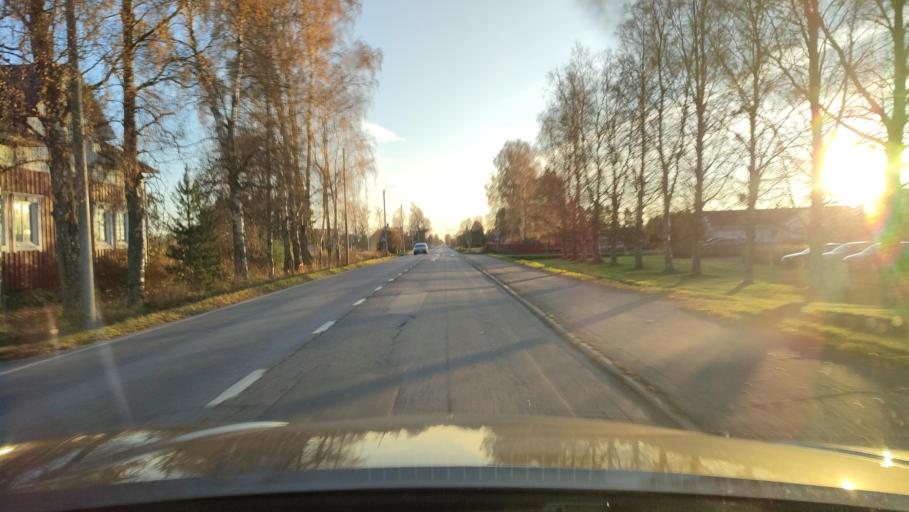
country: FI
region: Ostrobothnia
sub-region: Sydosterbotten
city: Naerpes
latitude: 62.5411
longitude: 21.3924
